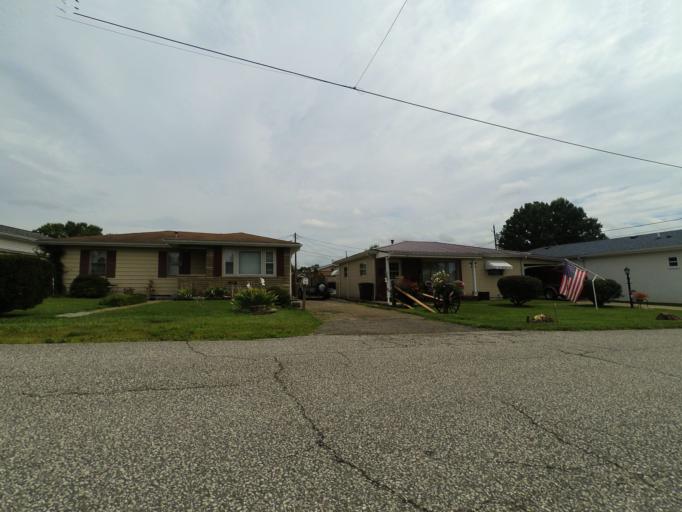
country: US
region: West Virginia
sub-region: Cabell County
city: Huntington
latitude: 38.4228
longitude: -82.4779
